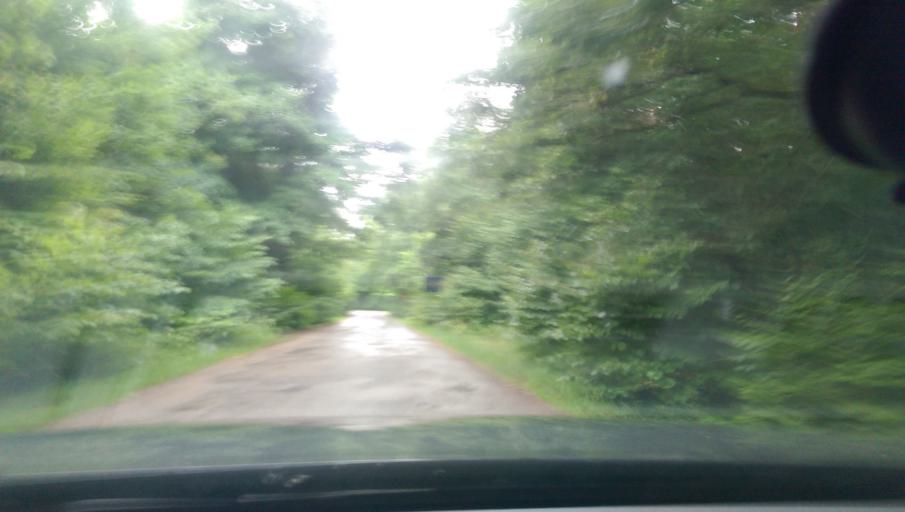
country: PL
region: Warmian-Masurian Voivodeship
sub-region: Powiat mragowski
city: Piecki
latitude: 53.7236
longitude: 21.4161
